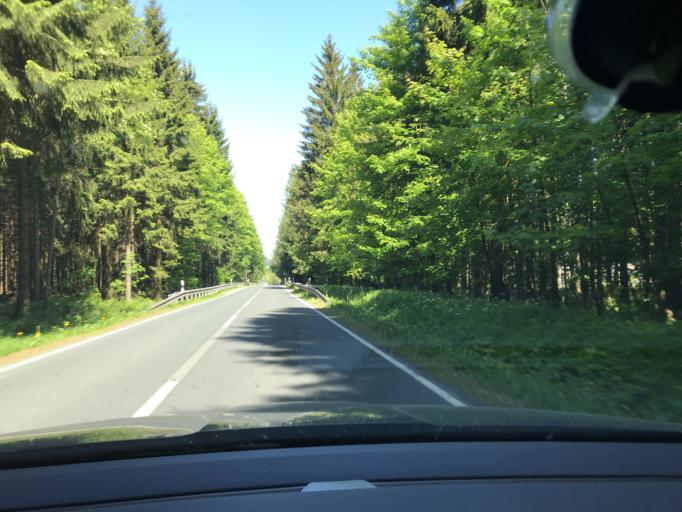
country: CZ
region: Ustecky
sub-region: Okres Chomutov
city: Vejprty
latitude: 50.4629
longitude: 12.9934
